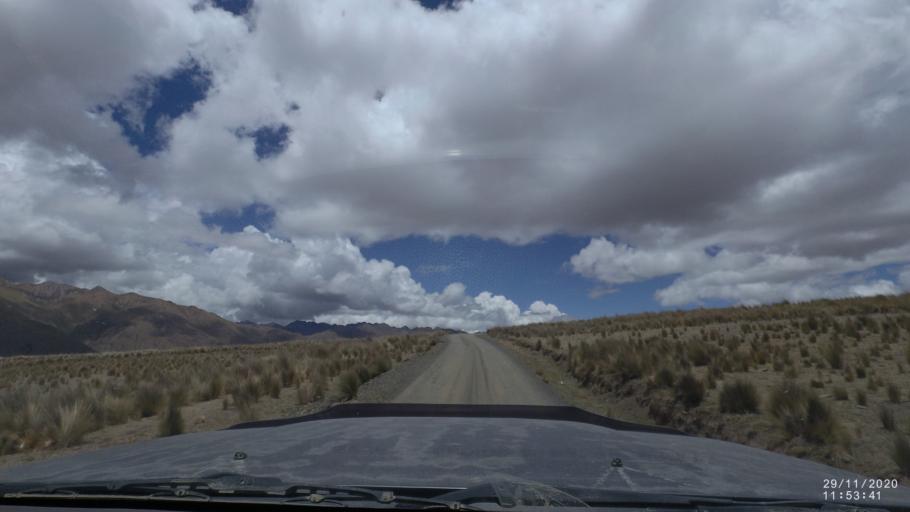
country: BO
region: Cochabamba
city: Cochabamba
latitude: -17.1650
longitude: -66.2694
